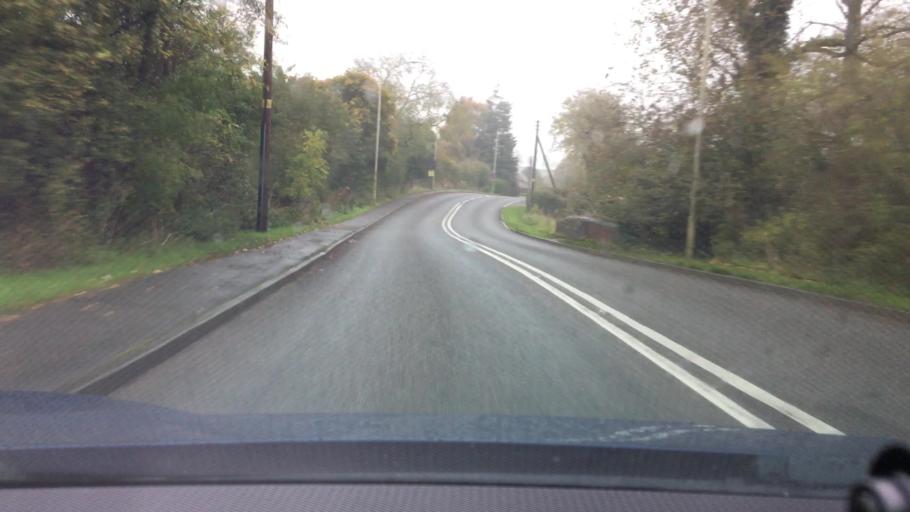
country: GB
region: England
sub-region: Leicestershire
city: Market Harborough
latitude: 52.4771
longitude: -0.9692
